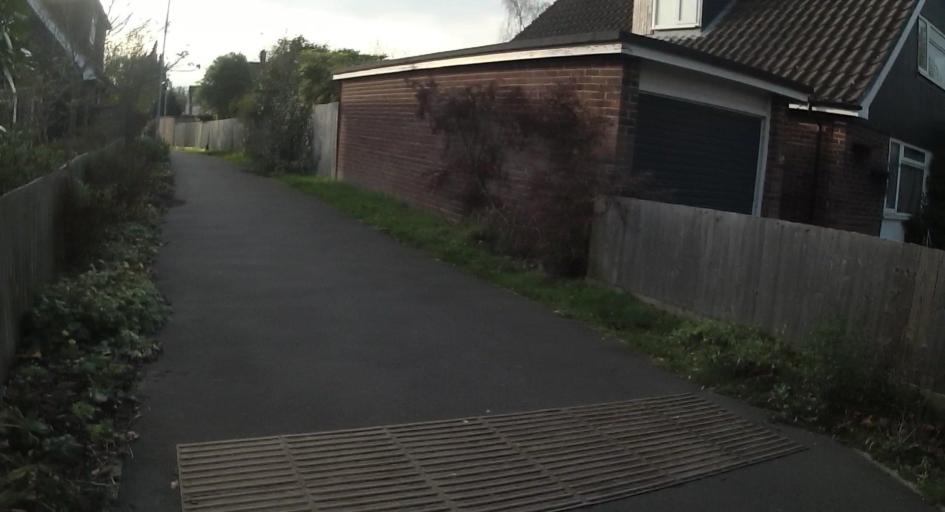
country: GB
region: England
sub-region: Wokingham
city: Wokingham
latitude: 51.4208
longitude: -0.8468
